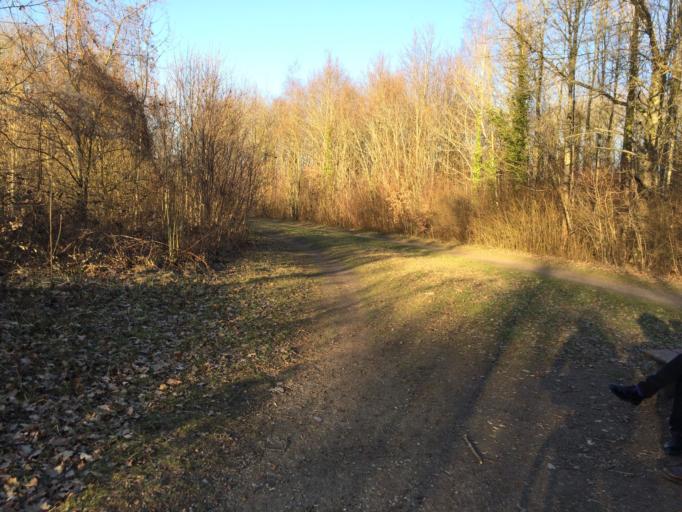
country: FR
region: Ile-de-France
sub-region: Departement de l'Essonne
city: Villebon-sur-Yvette
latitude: 48.7174
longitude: 2.2291
